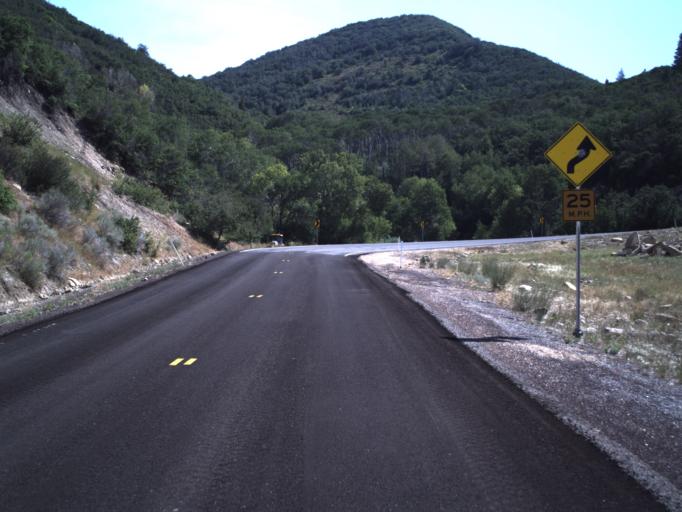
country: US
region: Utah
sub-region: Sanpete County
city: Fairview
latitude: 39.6483
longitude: -111.3765
